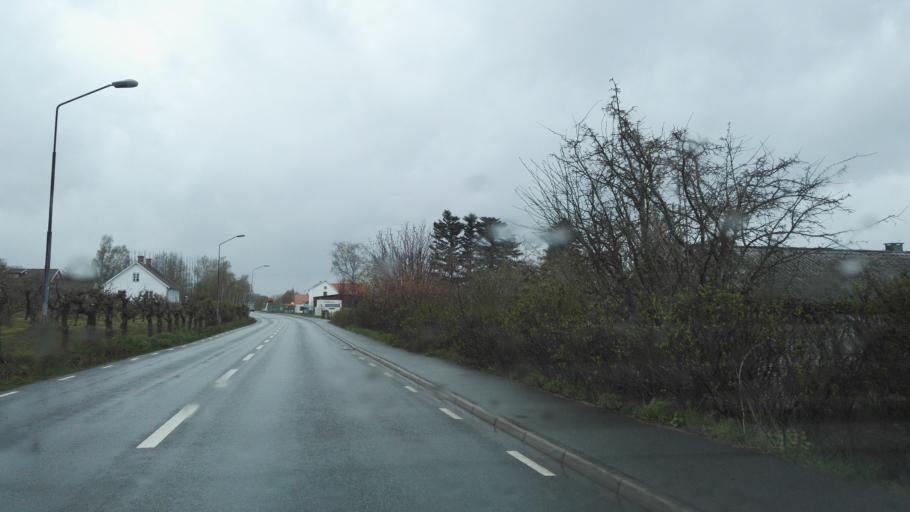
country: SE
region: Skane
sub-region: Simrishamns Kommun
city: Kivik
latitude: 55.6824
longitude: 14.2254
